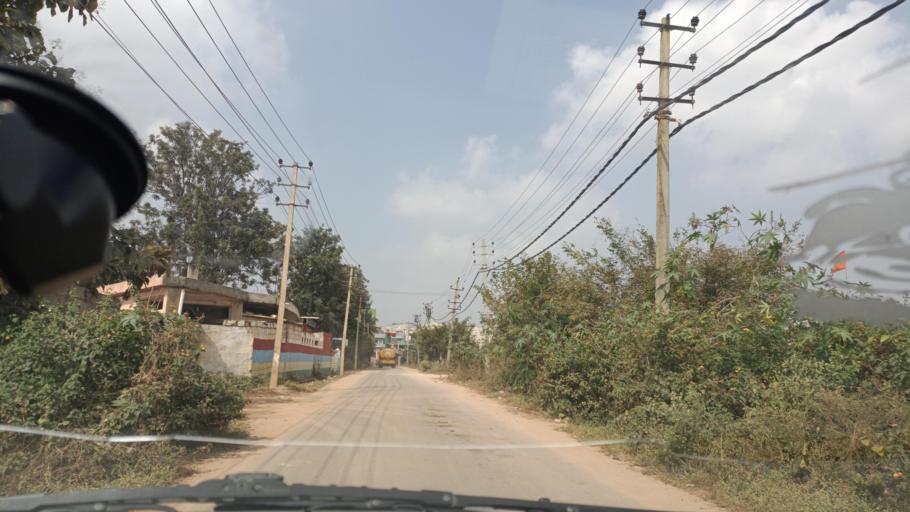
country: IN
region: Karnataka
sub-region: Bangalore Urban
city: Yelahanka
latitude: 13.1536
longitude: 77.6276
